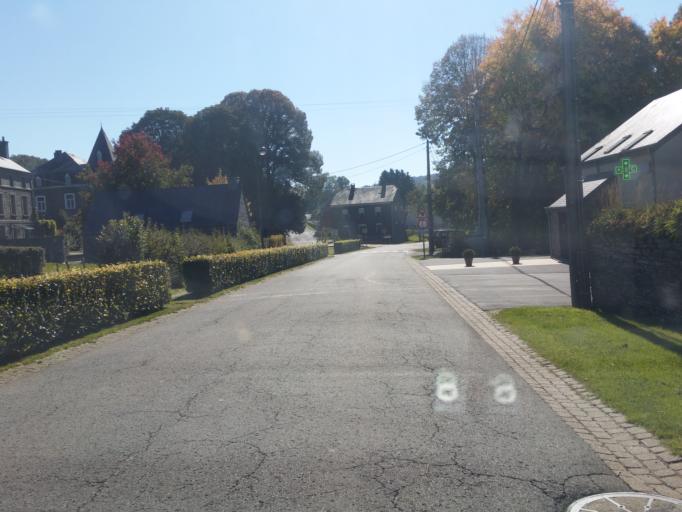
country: BE
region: Wallonia
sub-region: Province du Luxembourg
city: Herbeumont
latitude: 49.7785
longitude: 5.2392
